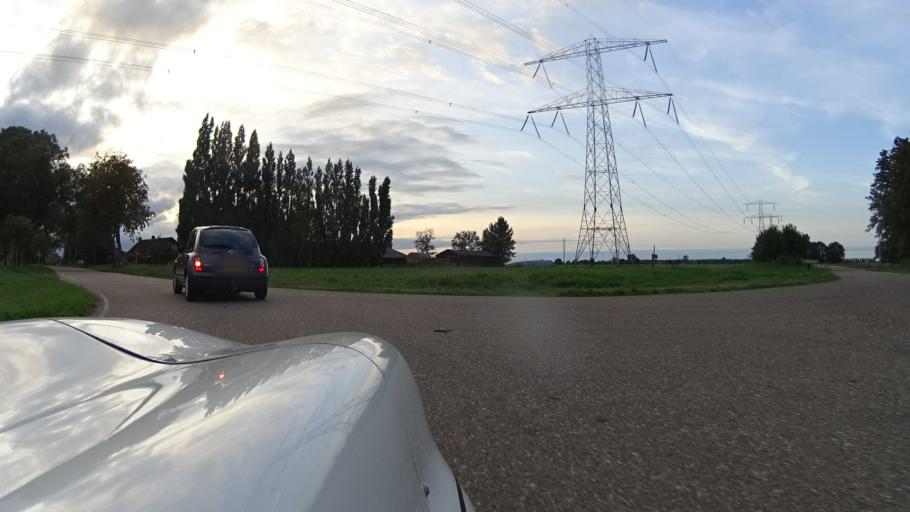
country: NL
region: South Holland
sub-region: Gemeente Sliedrecht
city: Sliedrecht
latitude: 51.8330
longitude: 4.8042
